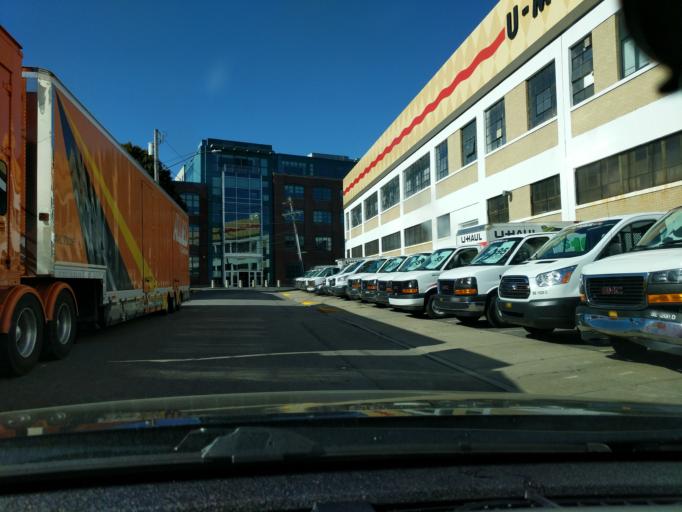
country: US
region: Massachusetts
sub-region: Suffolk County
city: South Boston
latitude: 42.3289
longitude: -71.0694
